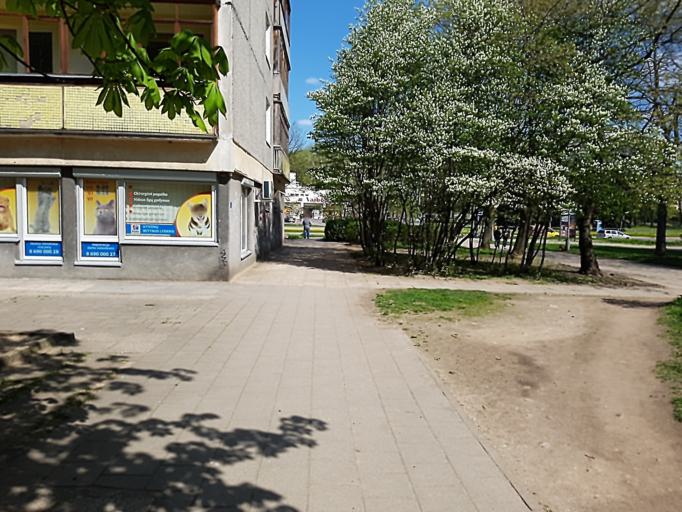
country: LT
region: Vilnius County
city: Lazdynai
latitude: 54.6773
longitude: 25.2130
